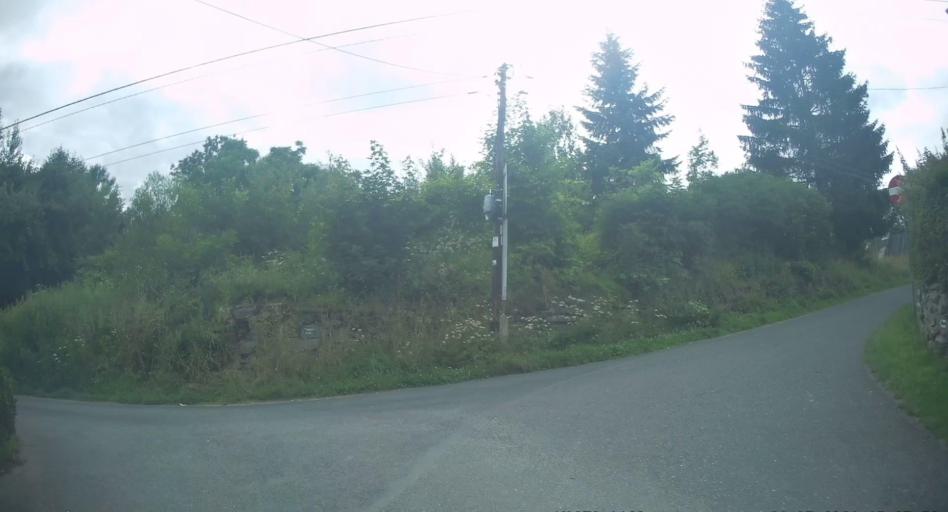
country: PL
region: Lower Silesian Voivodeship
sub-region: Powiat kamiennogorski
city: Marciszow
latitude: 50.8355
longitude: 15.9741
